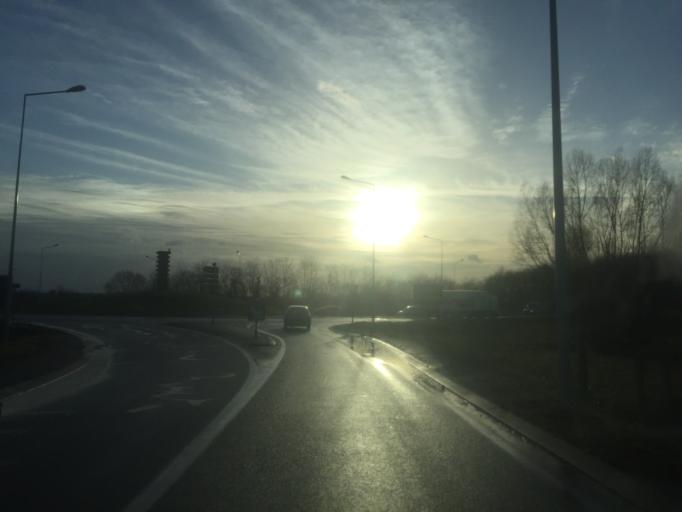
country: FR
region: Franche-Comte
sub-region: Departement du Jura
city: Dampierre
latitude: 47.1518
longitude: 5.7189
